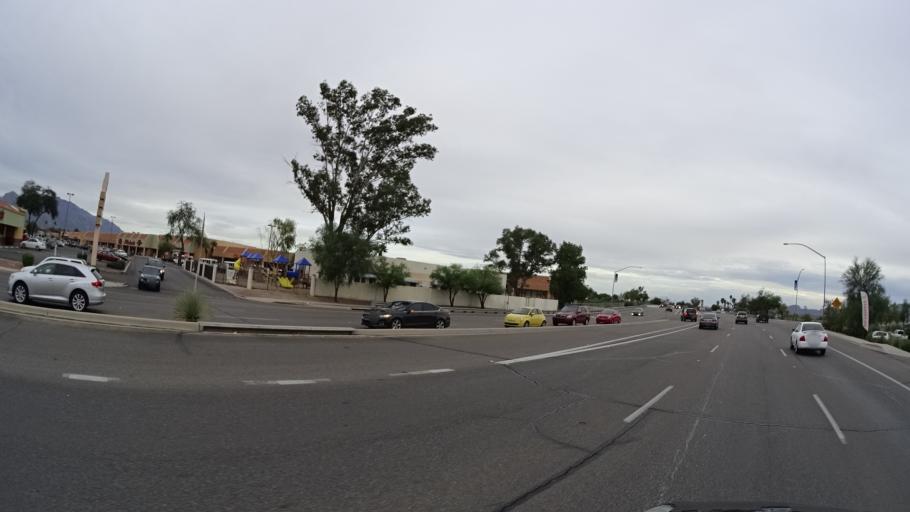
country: US
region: Arizona
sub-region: Pima County
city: Casas Adobes
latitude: 32.3359
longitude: -111.0468
